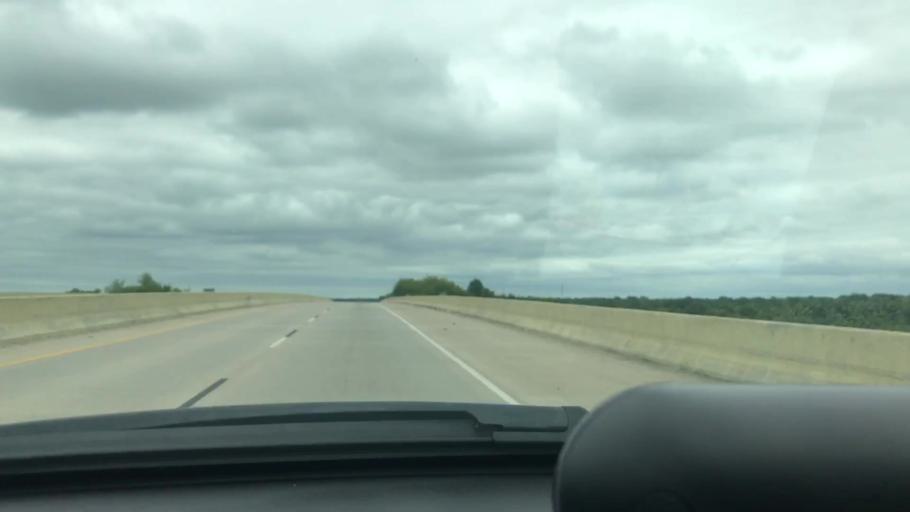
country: US
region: Oklahoma
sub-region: Wagoner County
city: Wagoner
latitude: 35.8849
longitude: -95.4026
